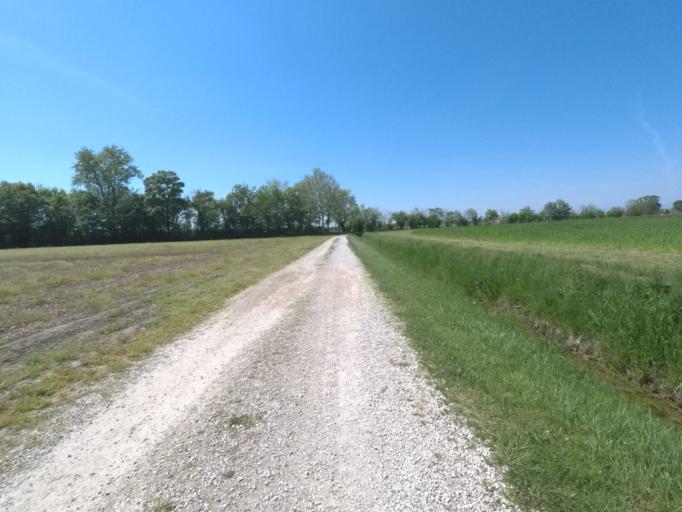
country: IT
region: Veneto
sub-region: Provincia di Treviso
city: Piavon
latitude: 45.7852
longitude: 12.5248
